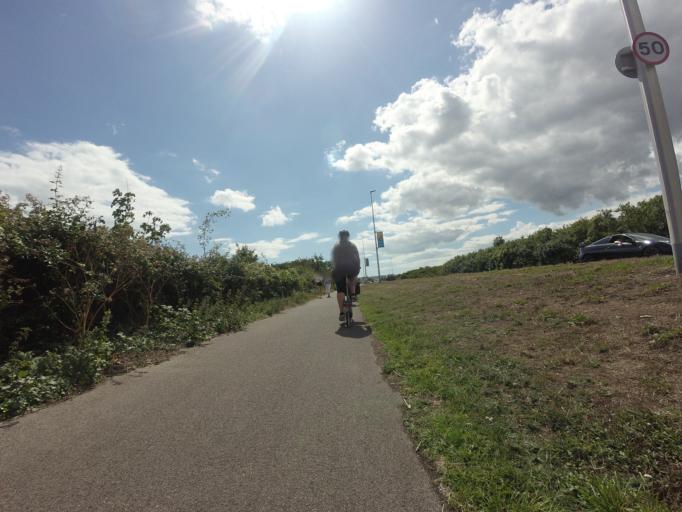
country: GB
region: England
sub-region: East Sussex
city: Pevensey
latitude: 50.8004
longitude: 0.3301
